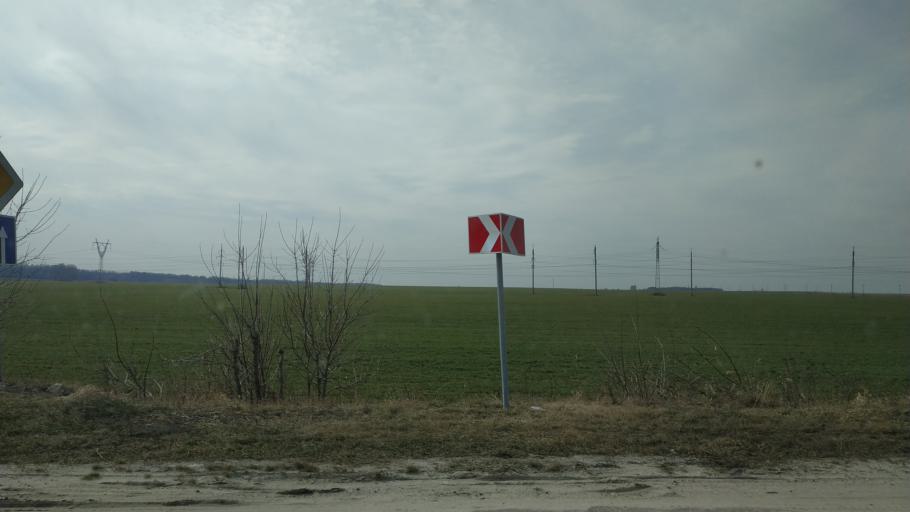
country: RU
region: Moskovskaya
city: Voskresensk
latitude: 55.2888
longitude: 38.6793
